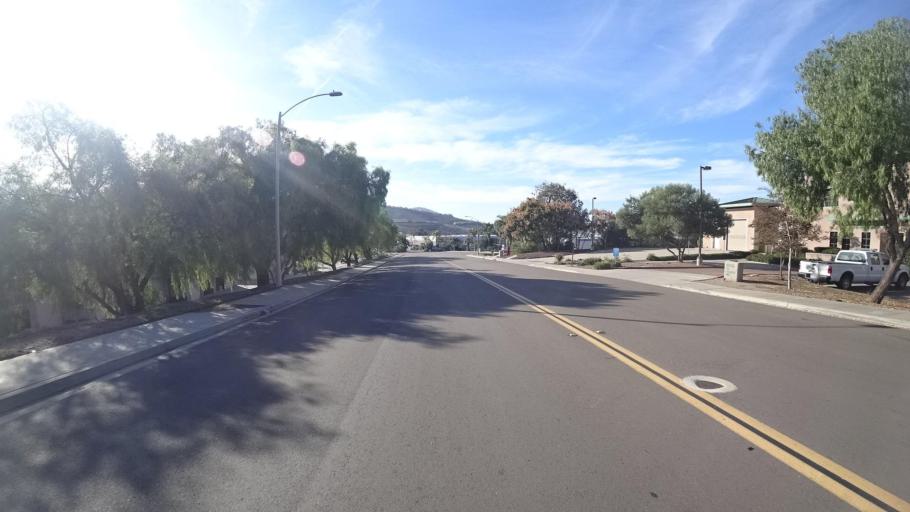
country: US
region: California
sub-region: San Diego County
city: Spring Valley
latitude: 32.7303
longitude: -116.9691
